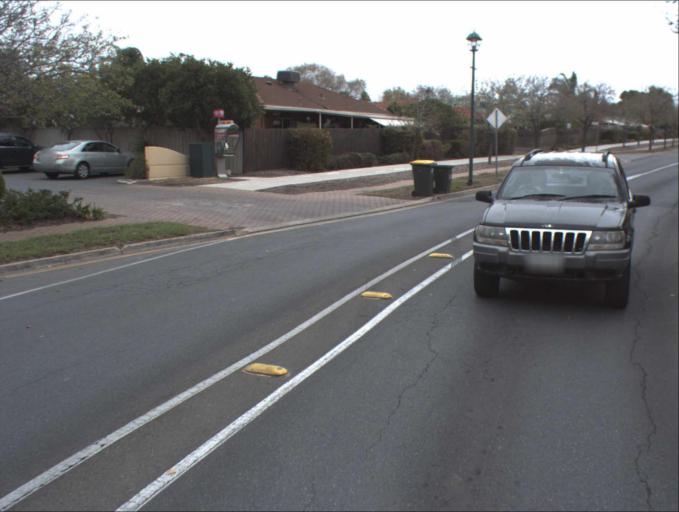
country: AU
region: South Australia
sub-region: Port Adelaide Enfield
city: Gilles Plains
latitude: -34.8547
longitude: 138.6457
